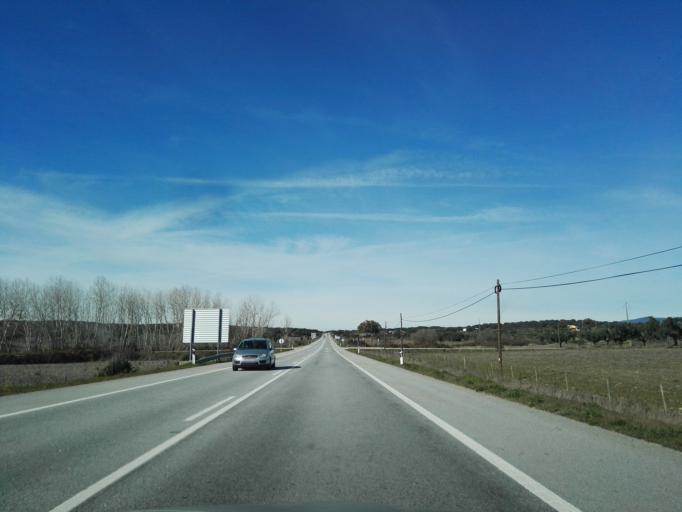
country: PT
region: Portalegre
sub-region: Arronches
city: Arronches
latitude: 39.1593
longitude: -7.3201
